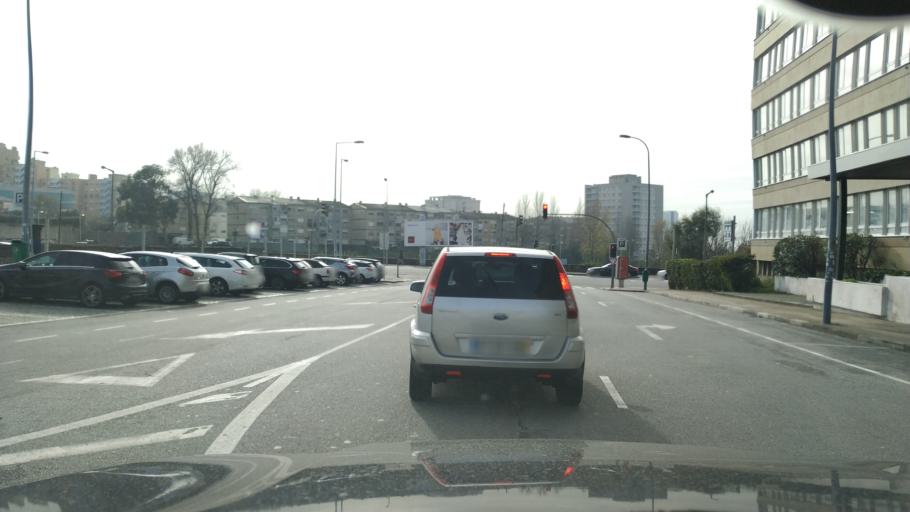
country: PT
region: Porto
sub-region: Matosinhos
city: Senhora da Hora
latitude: 41.1615
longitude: -8.6464
